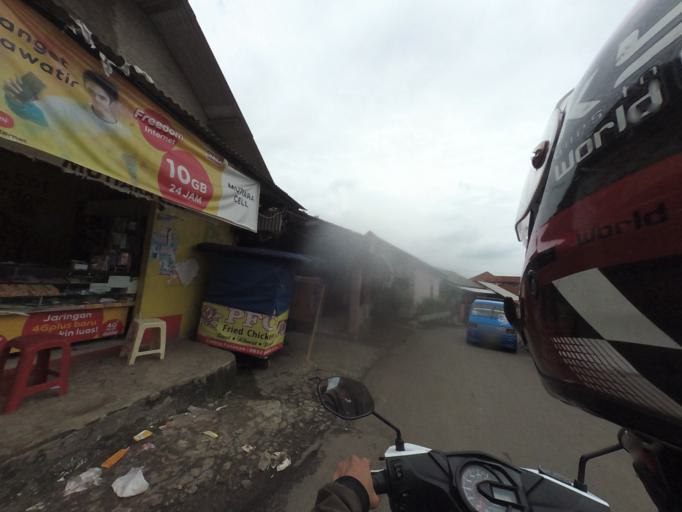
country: ID
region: West Java
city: Bogor
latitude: -6.6196
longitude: 106.7464
